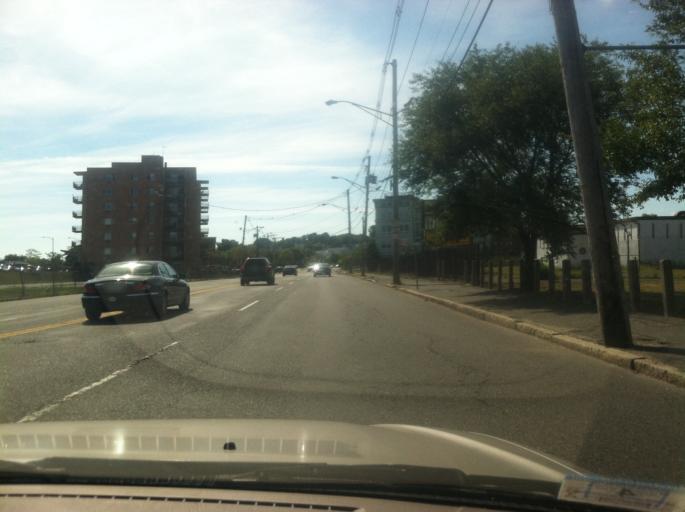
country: US
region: Massachusetts
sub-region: Suffolk County
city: Revere
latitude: 42.4039
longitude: -70.9915
